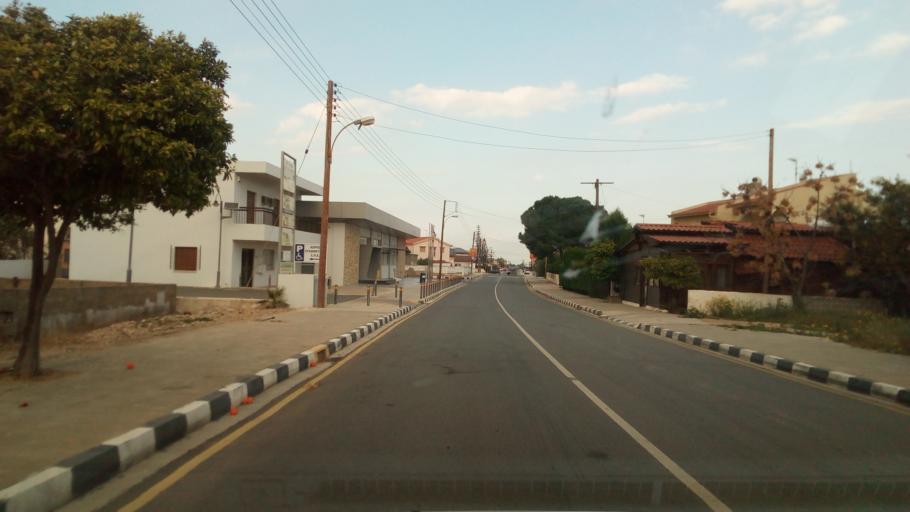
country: CY
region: Larnaka
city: Xylotymbou
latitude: 35.0189
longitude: 33.7449
